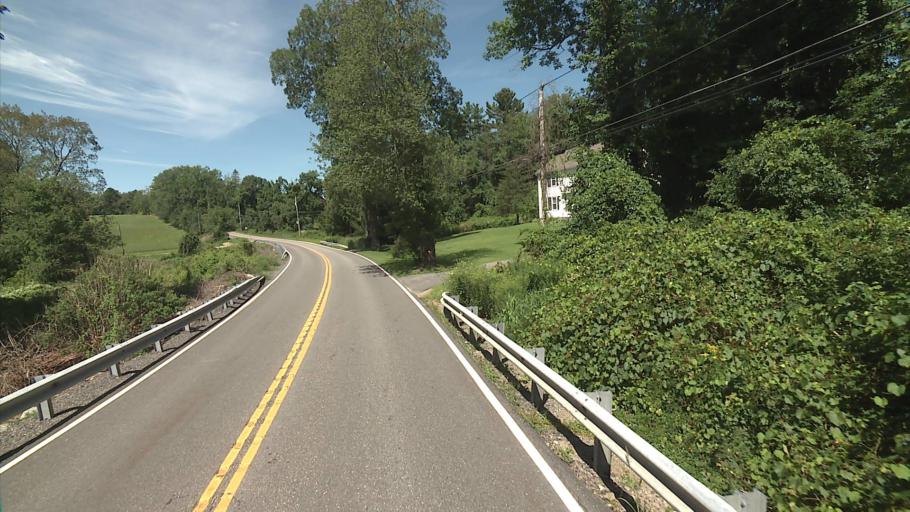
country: US
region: Connecticut
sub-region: Windham County
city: South Woodstock
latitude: 41.8986
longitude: -71.9967
